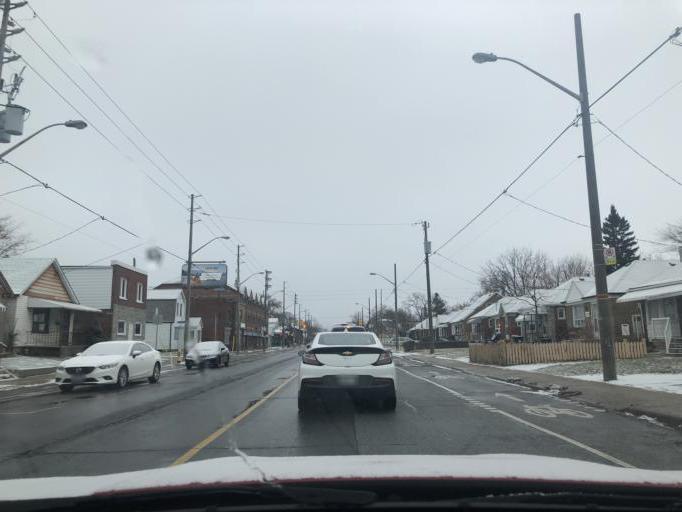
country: CA
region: Ontario
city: Scarborough
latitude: 43.6977
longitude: -79.3179
